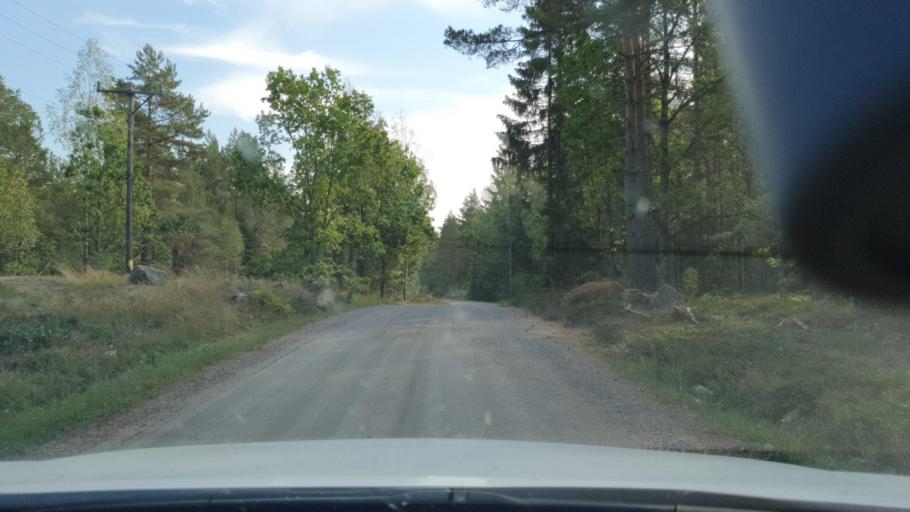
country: SE
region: Kalmar
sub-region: Vasterviks Kommun
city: Ankarsrum
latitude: 57.6972
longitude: 16.4617
